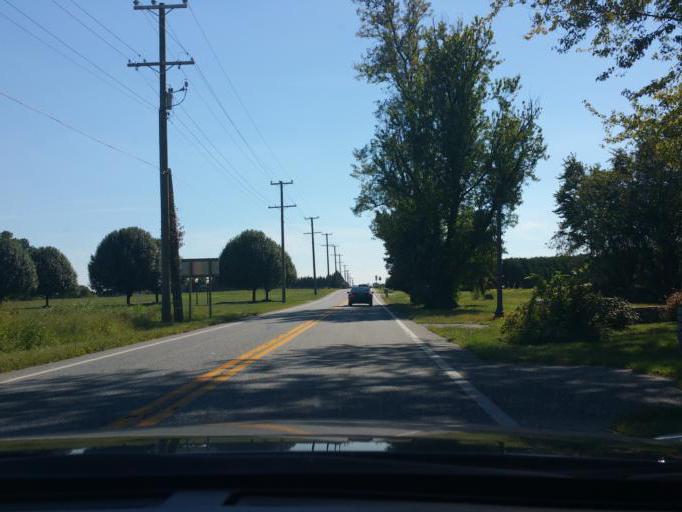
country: US
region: Maryland
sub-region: Harford County
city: Aberdeen
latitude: 39.5814
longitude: -76.1851
